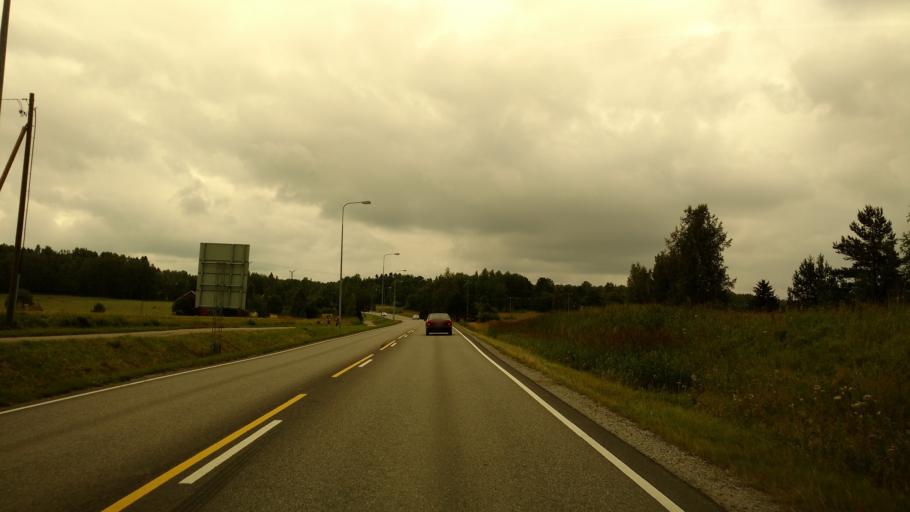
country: FI
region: Varsinais-Suomi
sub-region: Salo
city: Halikko
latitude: 60.4298
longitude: 23.0477
